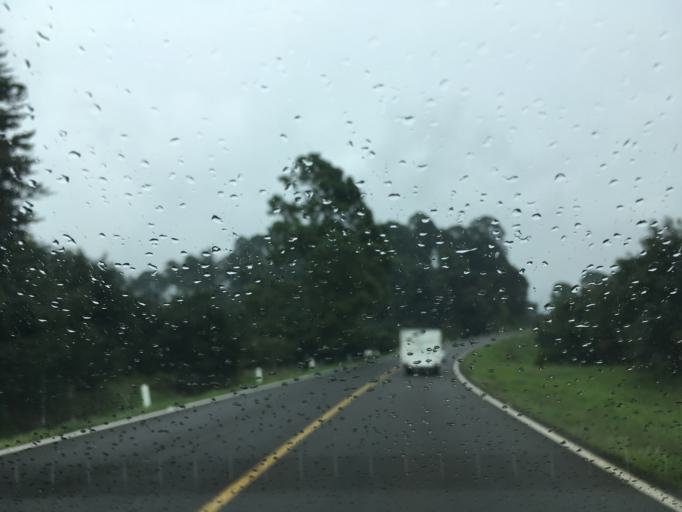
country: MX
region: Michoacan
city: Tingambato
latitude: 19.4935
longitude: -101.8757
